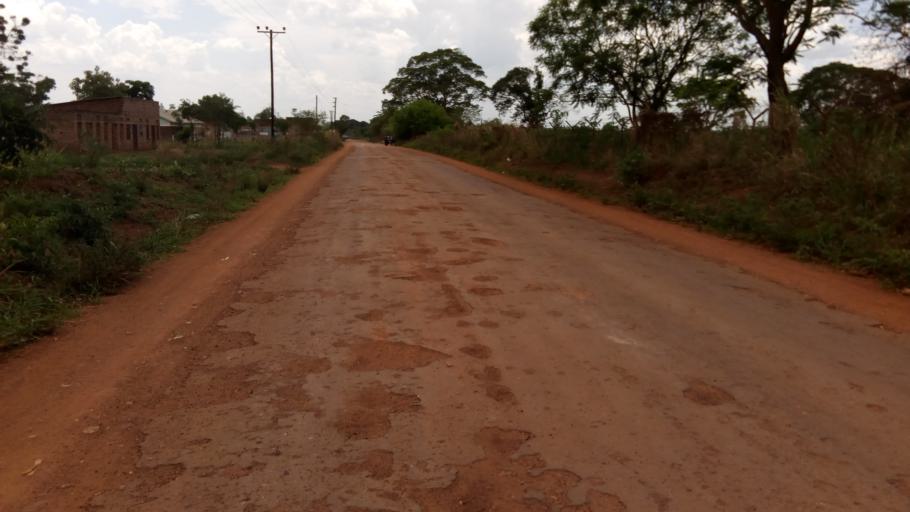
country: UG
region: Northern Region
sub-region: Gulu District
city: Gulu
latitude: 2.7872
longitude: 32.3478
